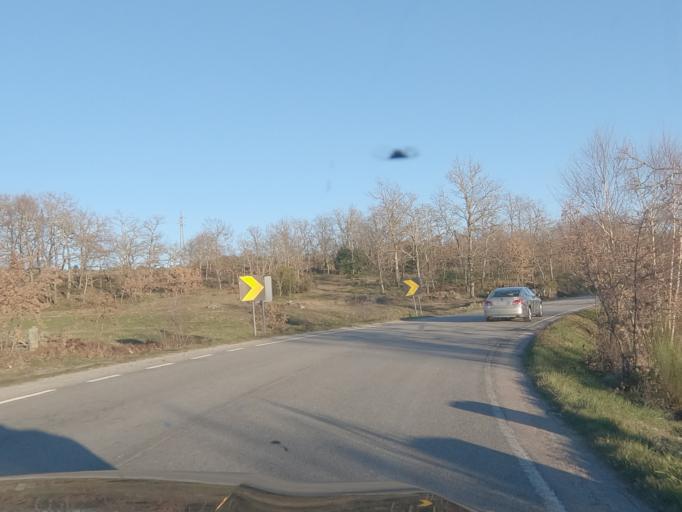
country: PT
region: Vila Real
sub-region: Ribeira de Pena
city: Ribeira de Pena
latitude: 41.5008
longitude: -7.7360
